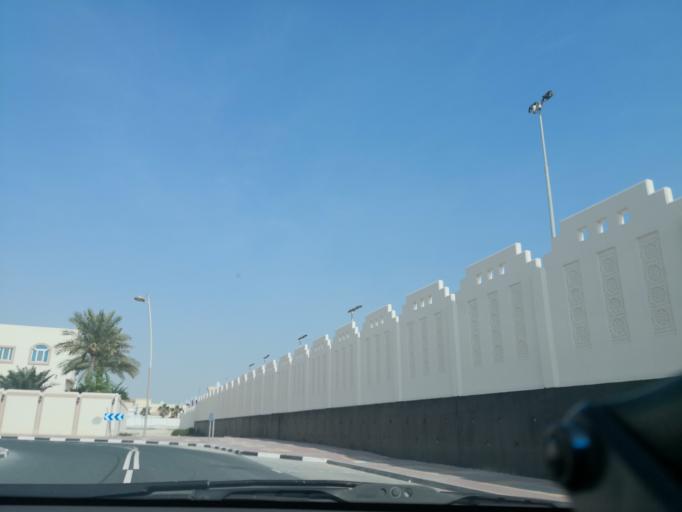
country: QA
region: Baladiyat ad Dawhah
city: Doha
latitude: 25.3447
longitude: 51.4942
